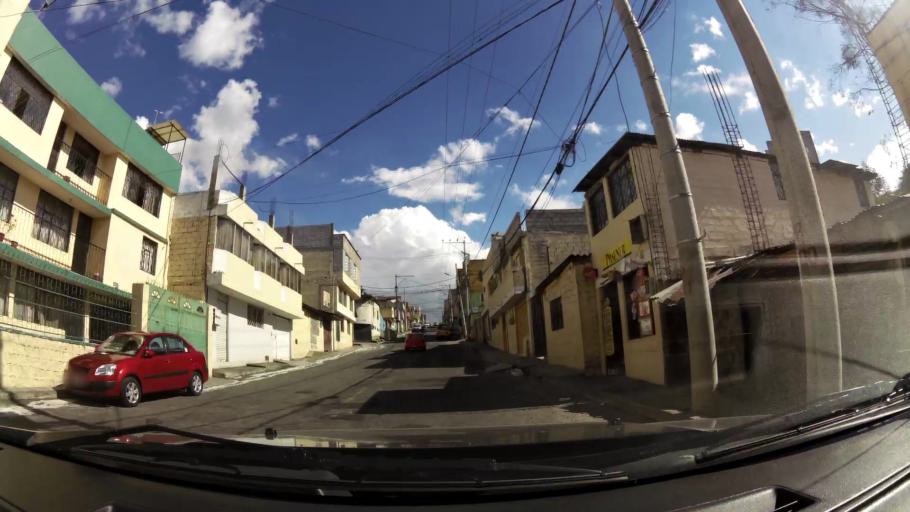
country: EC
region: Pichincha
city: Quito
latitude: -0.1186
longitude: -78.4688
